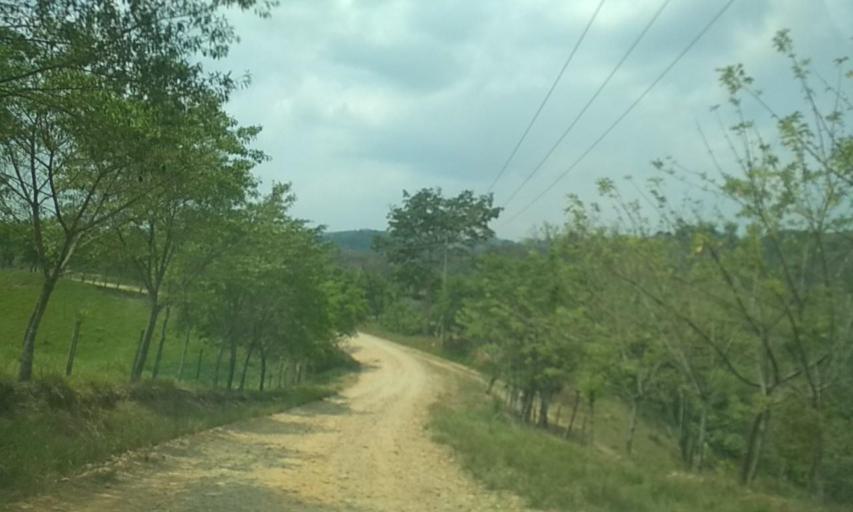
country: MX
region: Tabasco
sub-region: Huimanguillo
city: Francisco Rueda
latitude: 17.6090
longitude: -93.8076
